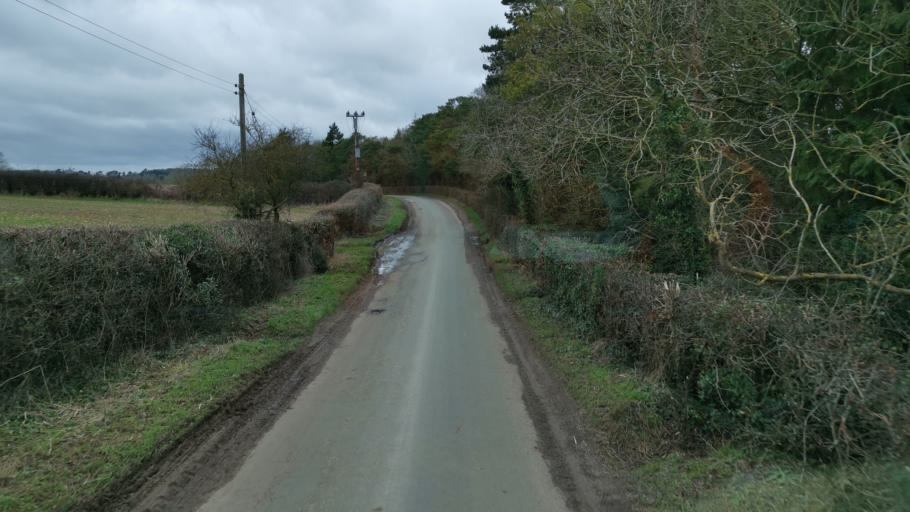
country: GB
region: England
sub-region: Oxfordshire
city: Somerton
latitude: 51.8993
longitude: -1.3087
